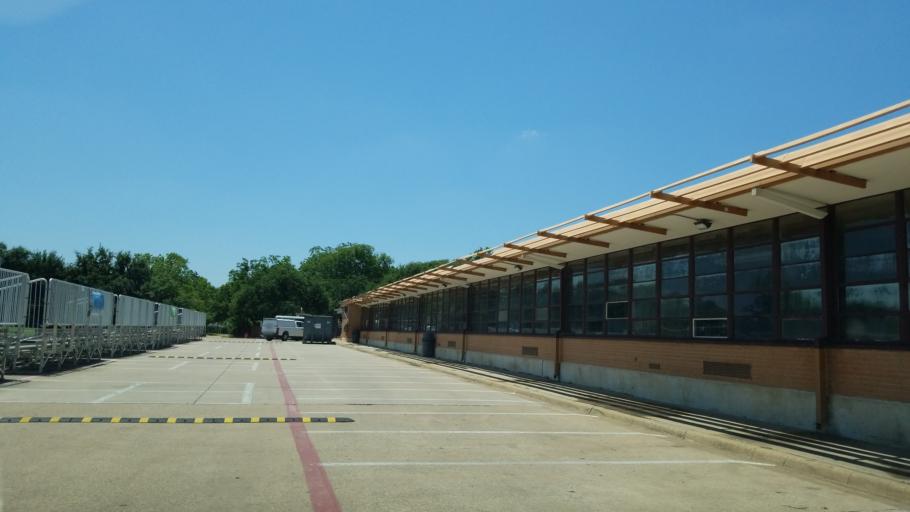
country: US
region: Texas
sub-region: Dallas County
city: University Park
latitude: 32.8790
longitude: -96.8399
